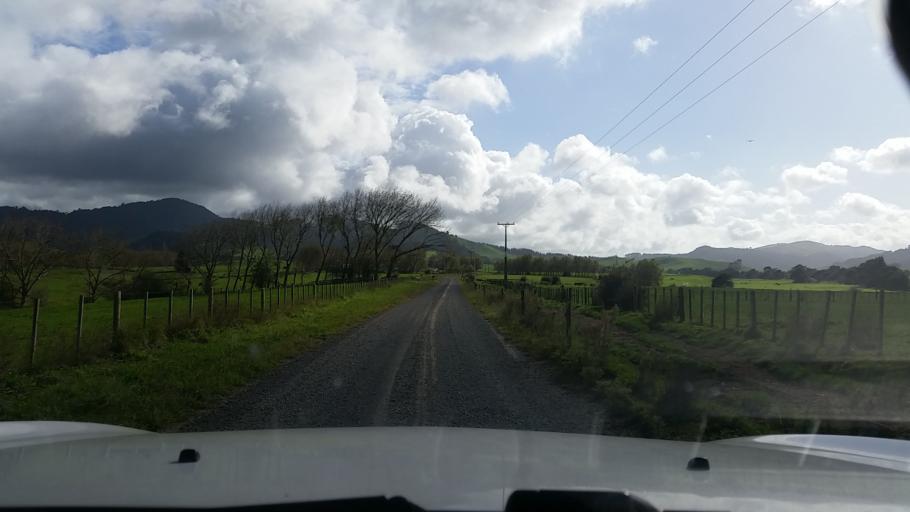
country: NZ
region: Waikato
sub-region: Hauraki District
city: Ngatea
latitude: -37.5085
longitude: 175.4074
